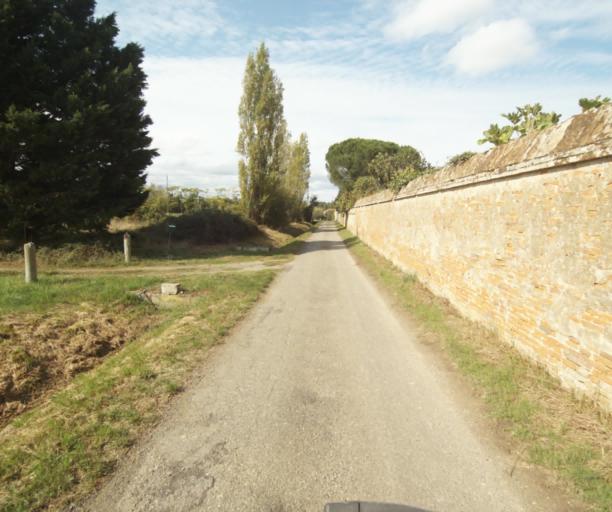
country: FR
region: Midi-Pyrenees
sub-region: Departement du Tarn-et-Garonne
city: Finhan
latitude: 43.8814
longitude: 1.1979
